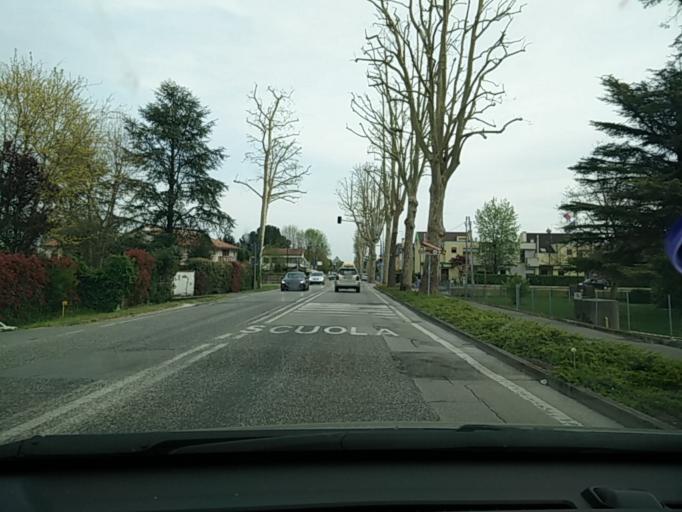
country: IT
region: Veneto
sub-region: Provincia di Venezia
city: Noventa di Piave
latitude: 45.6463
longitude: 12.5481
